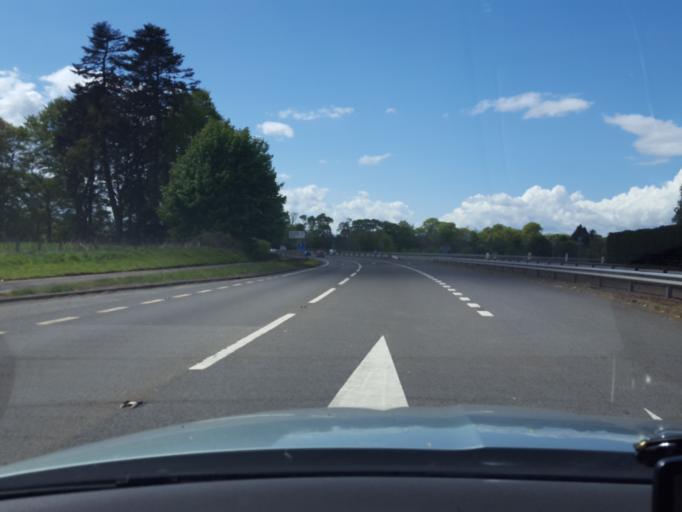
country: GB
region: Scotland
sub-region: Angus
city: Forfar
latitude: 56.7069
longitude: -2.8206
